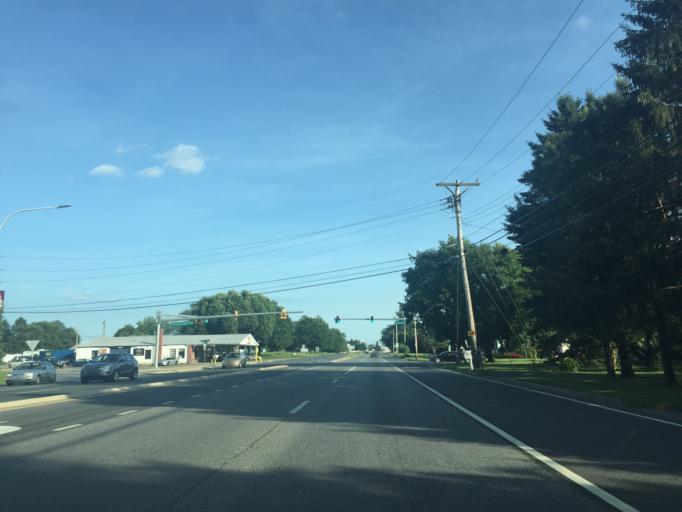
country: US
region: Delaware
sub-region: Kent County
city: Smyrna
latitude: 39.2921
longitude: -75.5970
